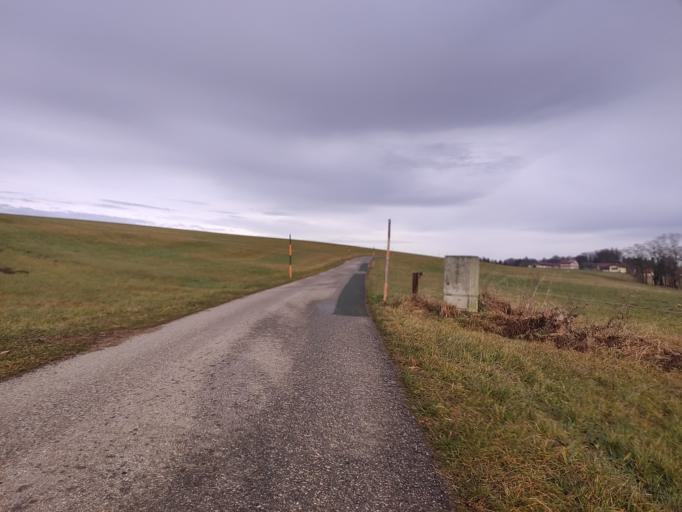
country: AT
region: Salzburg
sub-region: Politischer Bezirk Salzburg-Umgebung
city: Elixhausen
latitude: 47.8701
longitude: 13.0479
